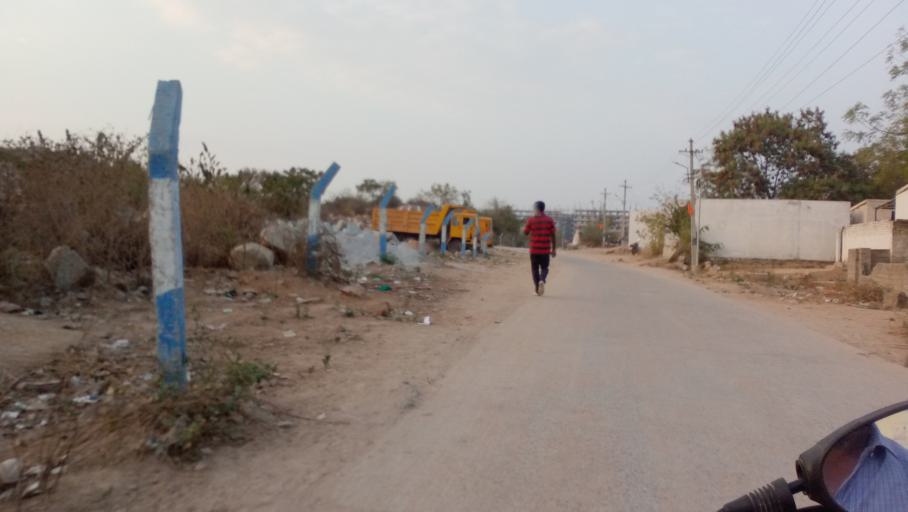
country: IN
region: Telangana
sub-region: Medak
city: Serilingampalle
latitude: 17.5195
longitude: 78.3087
